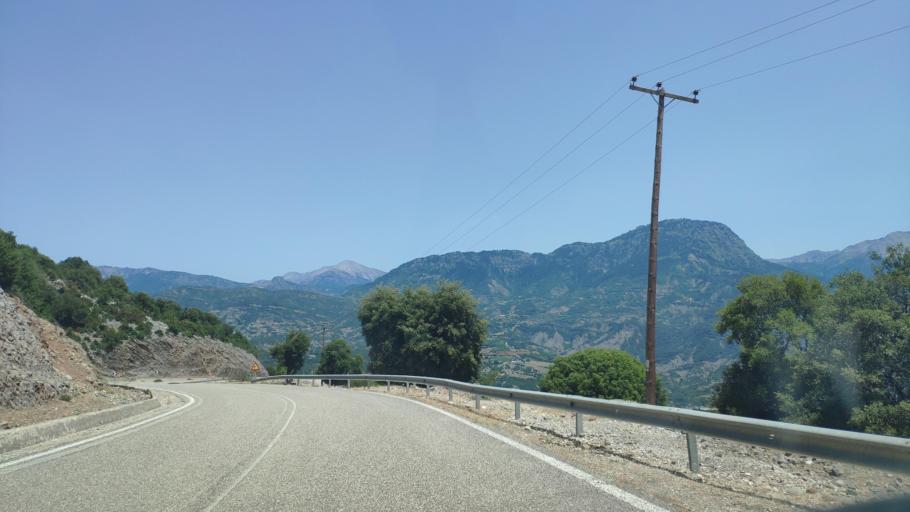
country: GR
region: Central Greece
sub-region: Nomos Evrytanias
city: Kerasochori
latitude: 39.0919
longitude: 21.4114
